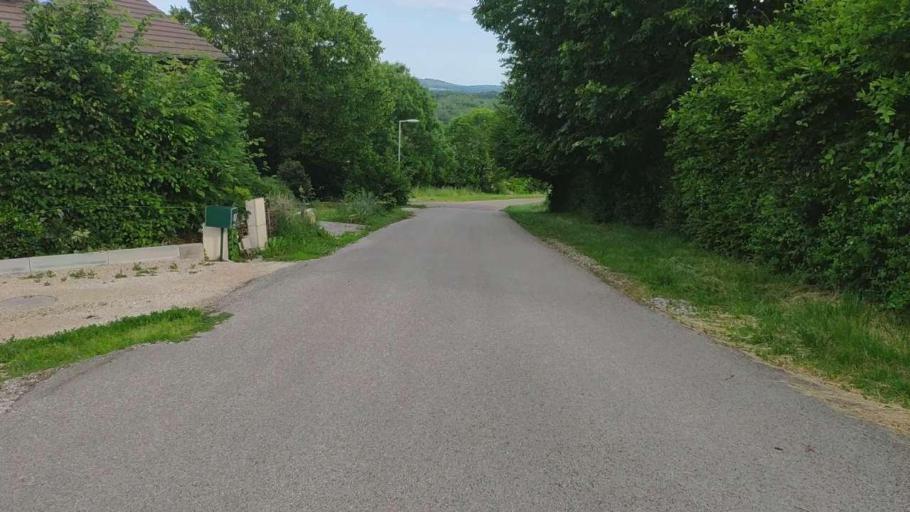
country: FR
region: Franche-Comte
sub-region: Departement du Jura
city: Perrigny
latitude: 46.7393
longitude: 5.6019
